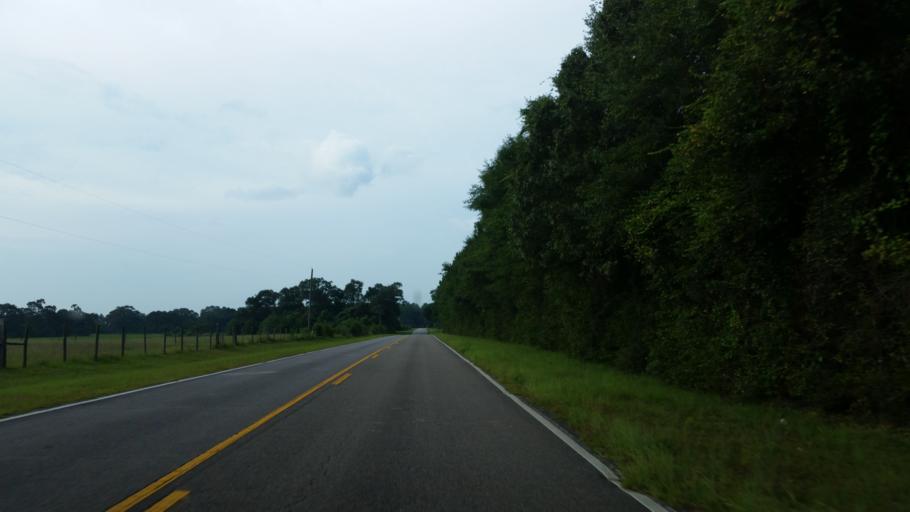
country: US
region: Florida
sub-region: Escambia County
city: Molino
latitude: 30.7779
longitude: -87.5240
